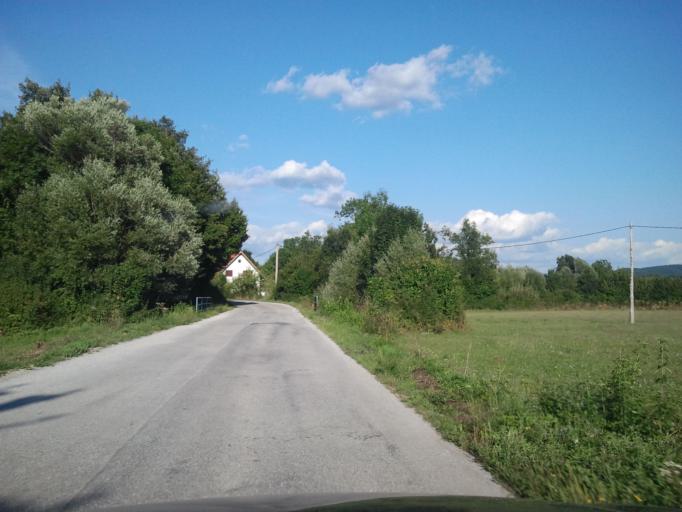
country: HR
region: Zadarska
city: Obrovac
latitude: 44.3502
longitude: 15.6379
